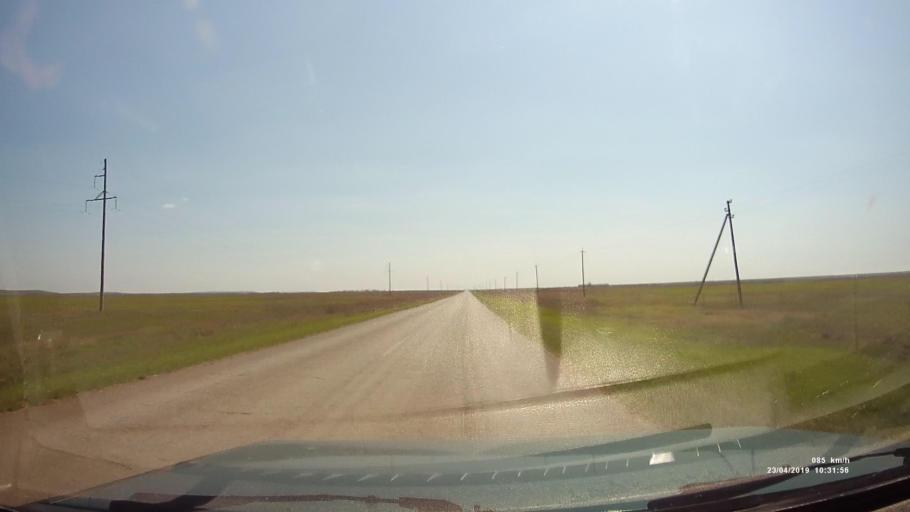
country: RU
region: Kalmykiya
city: Yashalta
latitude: 46.5833
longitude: 42.5693
